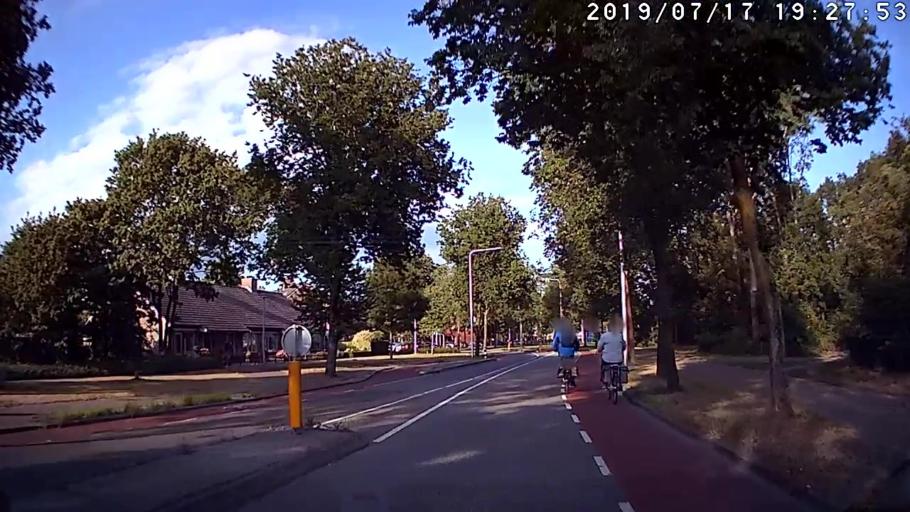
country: NL
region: Overijssel
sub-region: Gemeente Zwolle
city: Zwolle
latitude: 52.5356
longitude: 6.1068
